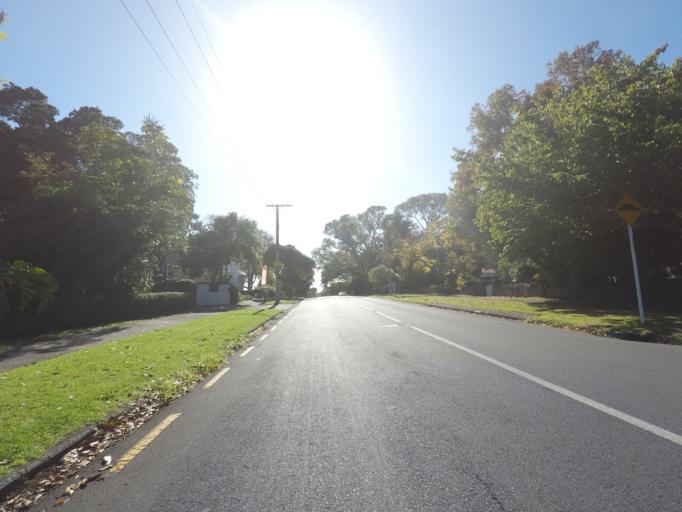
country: NZ
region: Auckland
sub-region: Auckland
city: Rosebank
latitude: -36.8888
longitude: 174.7138
